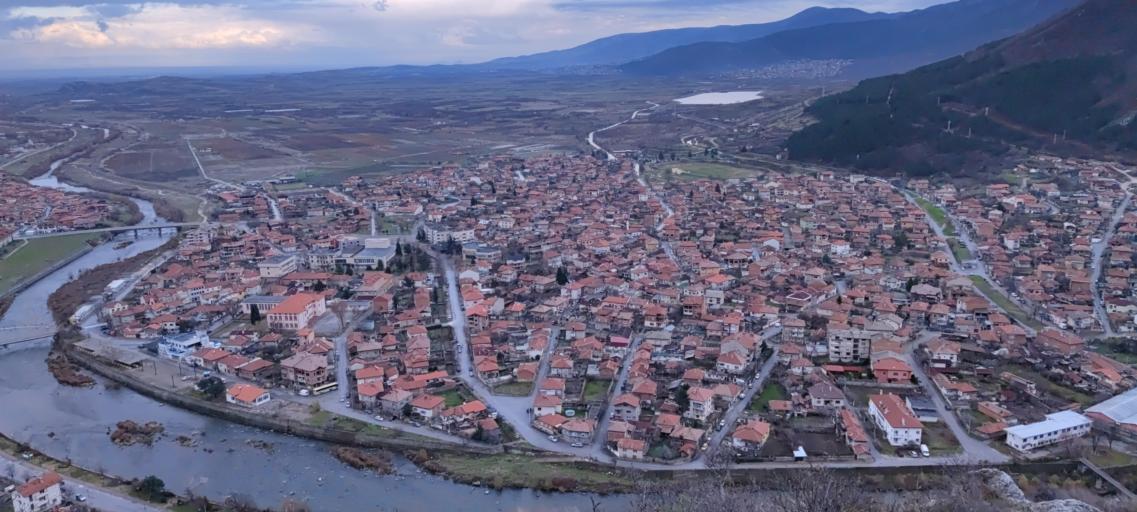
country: BG
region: Plovdiv
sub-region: Obshtina Krichim
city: Krichim
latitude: 42.0385
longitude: 24.4635
